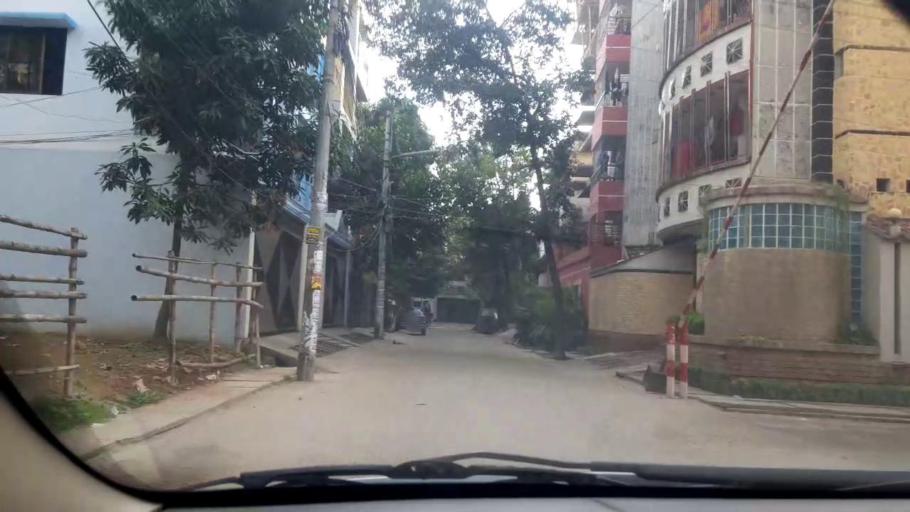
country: BD
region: Dhaka
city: Tungi
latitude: 23.8657
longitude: 90.3899
